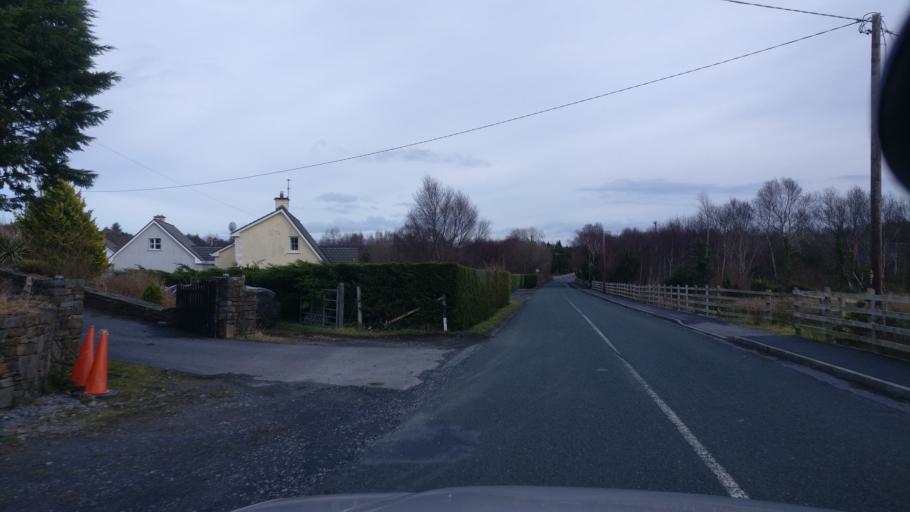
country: IE
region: Connaught
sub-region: County Galway
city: Oughterard
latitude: 53.5170
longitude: -9.4519
